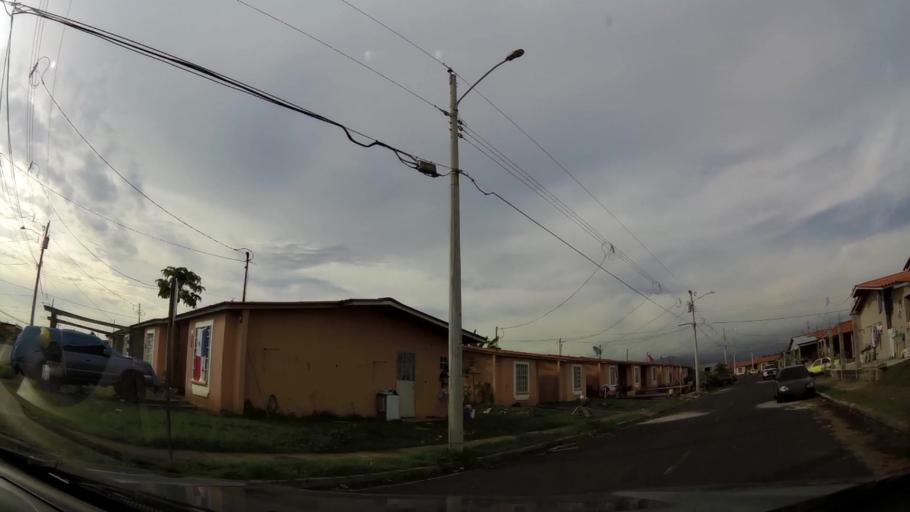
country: PA
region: Panama
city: Tocumen
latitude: 9.0691
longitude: -79.3610
